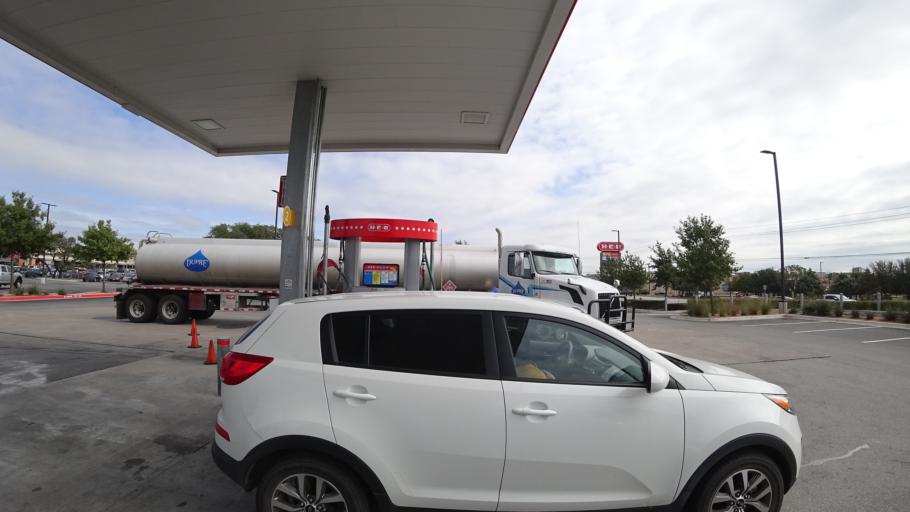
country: US
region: Texas
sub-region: Williamson County
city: Round Rock
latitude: 30.5596
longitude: -97.6887
